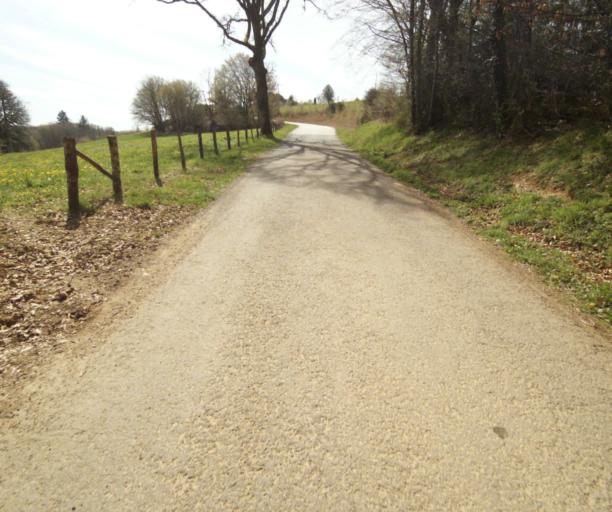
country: FR
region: Limousin
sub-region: Departement de la Correze
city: Naves
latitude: 45.3618
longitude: 1.7976
